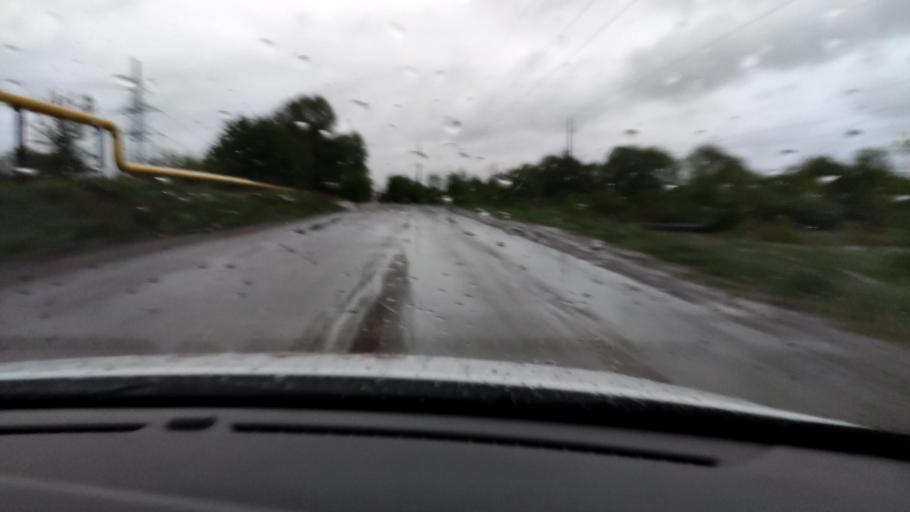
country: RU
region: Tatarstan
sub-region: Gorod Kazan'
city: Kazan
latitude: 55.7217
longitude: 49.1189
